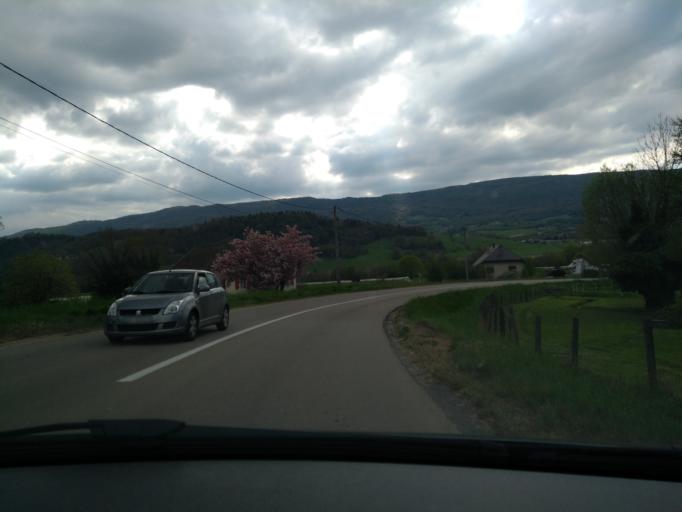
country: FR
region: Rhone-Alpes
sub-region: Departement de la Haute-Savoie
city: Vallieres
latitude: 45.9019
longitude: 5.9314
